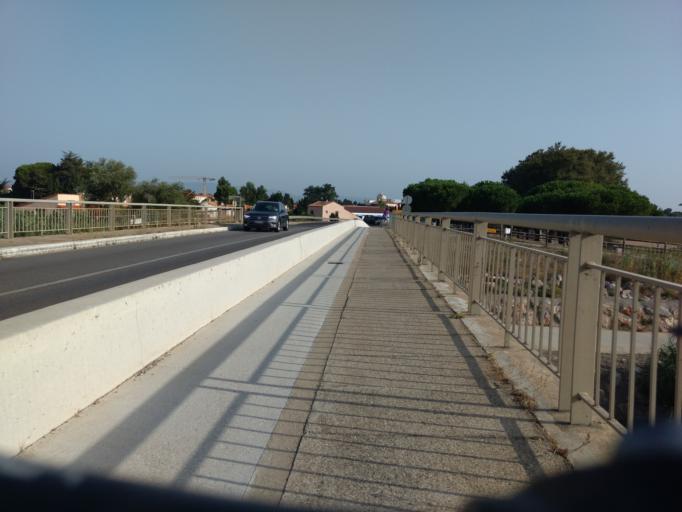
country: FR
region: Languedoc-Roussillon
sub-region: Departement des Pyrenees-Orientales
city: Saint-Laurent-de-la-Salanque
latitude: 42.7640
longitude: 2.9870
